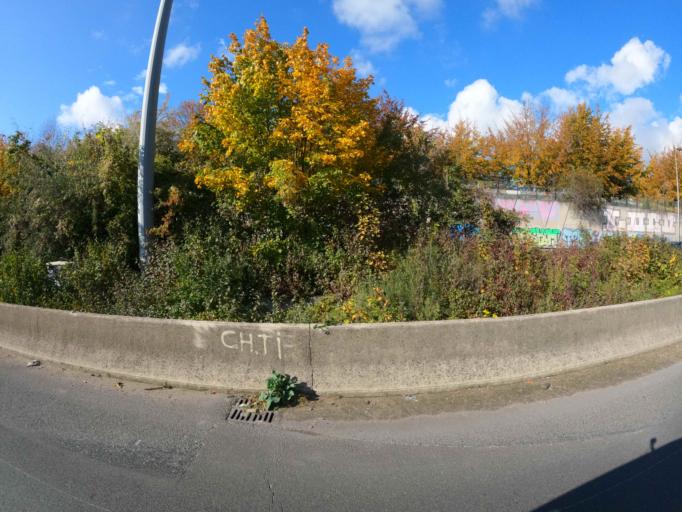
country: FR
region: Ile-de-France
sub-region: Departement du Val-de-Marne
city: Orly
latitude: 48.7538
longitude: 2.3819
